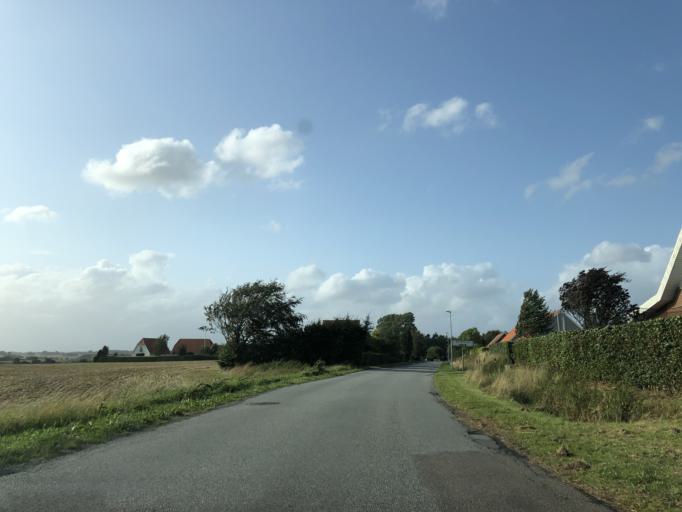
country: DK
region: South Denmark
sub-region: Haderslev Kommune
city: Starup
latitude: 55.1898
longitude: 9.5145
